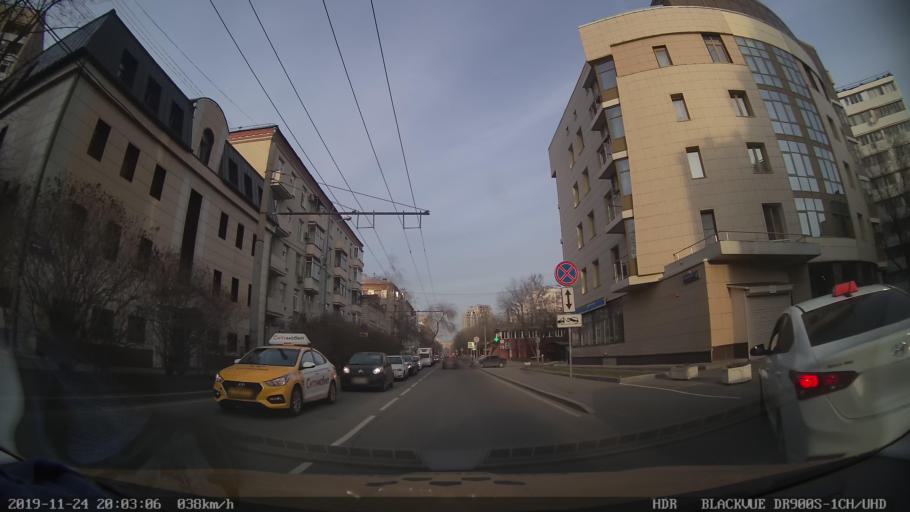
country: RU
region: Moscow
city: Mar'ina Roshcha
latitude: 55.7819
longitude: 37.5917
